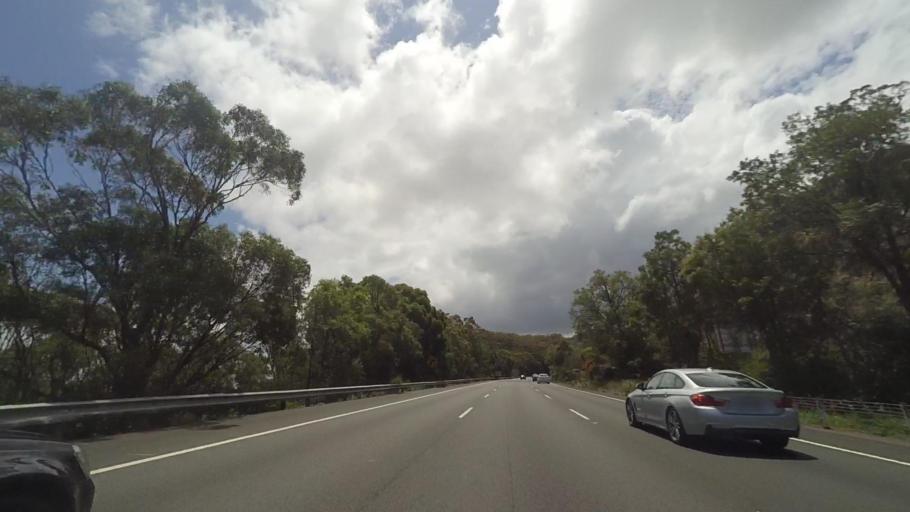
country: AU
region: New South Wales
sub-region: Hornsby Shire
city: Berowra Heights
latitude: -33.5259
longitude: 151.1970
